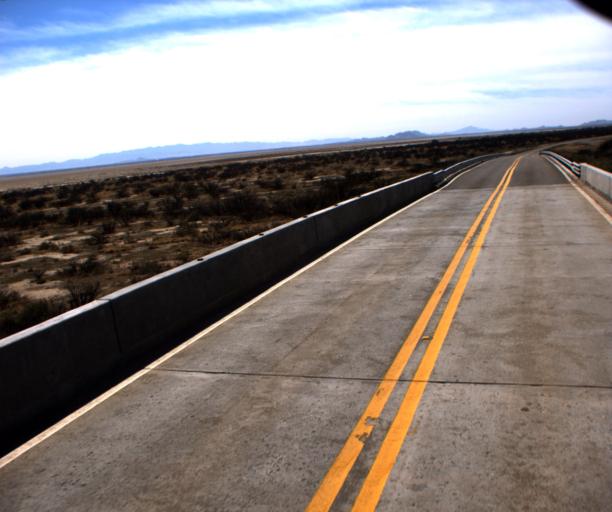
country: US
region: Arizona
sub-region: Cochise County
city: Willcox
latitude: 32.1337
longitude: -109.9108
